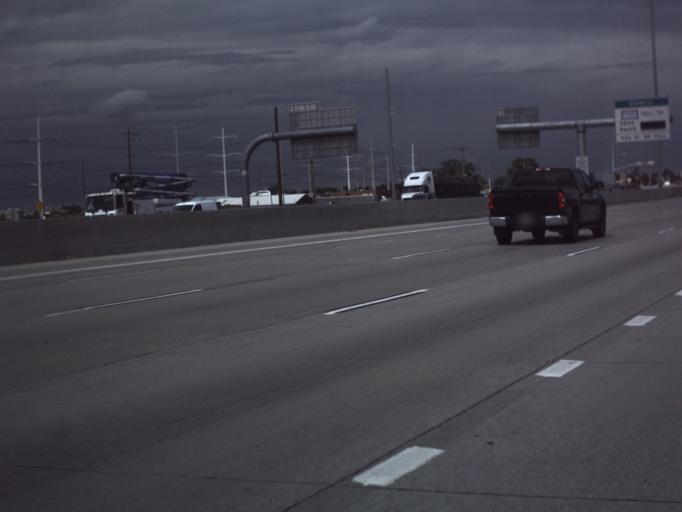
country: US
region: Utah
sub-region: Salt Lake County
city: Draper
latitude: 40.5208
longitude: -111.8908
